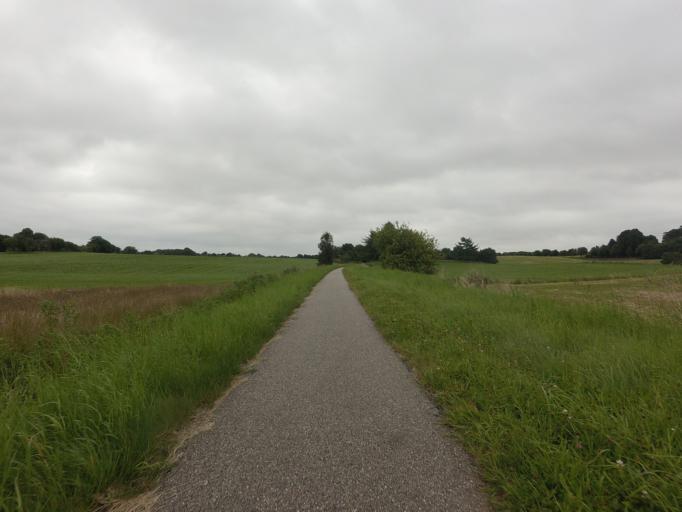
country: DK
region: Central Jutland
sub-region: Horsens Kommune
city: Braedstrup
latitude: 56.0252
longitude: 9.5547
